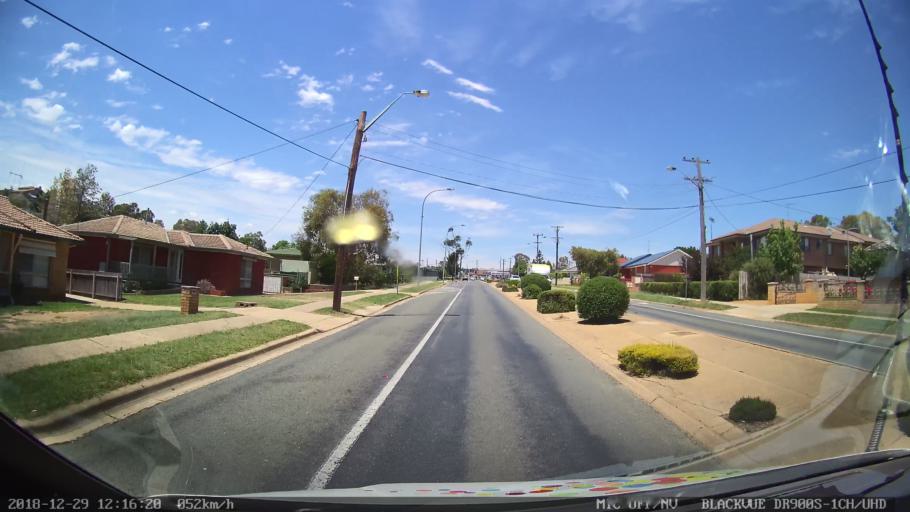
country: AU
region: New South Wales
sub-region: Queanbeyan
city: Queanbeyan
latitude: -35.3687
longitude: 149.2331
